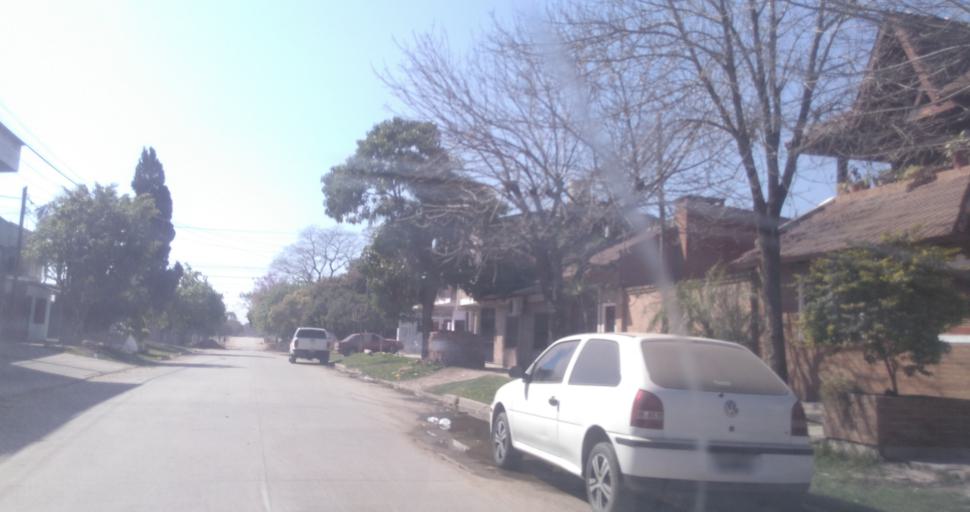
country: AR
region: Chaco
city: Fontana
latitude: -27.4282
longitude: -59.0258
